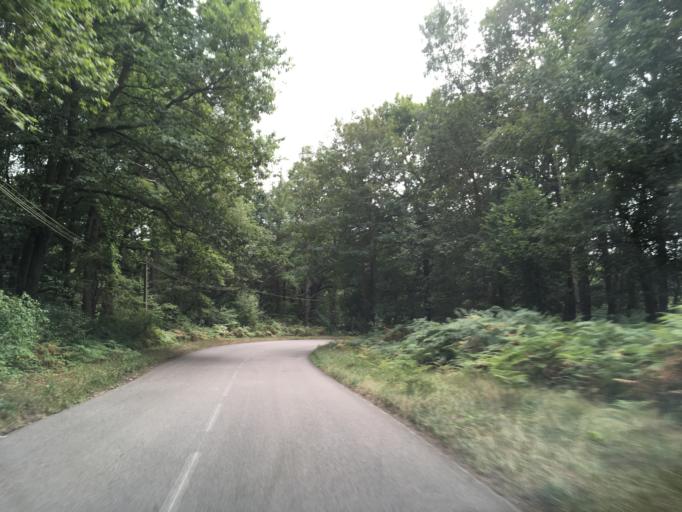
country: FR
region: Haute-Normandie
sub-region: Departement de l'Eure
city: Vernon
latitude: 49.1044
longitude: 1.5099
